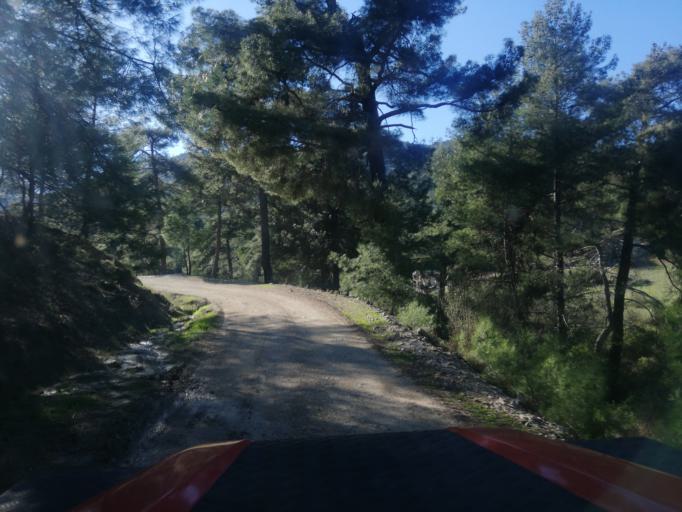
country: TR
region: Antalya
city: Kas
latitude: 36.2975
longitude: 29.6862
